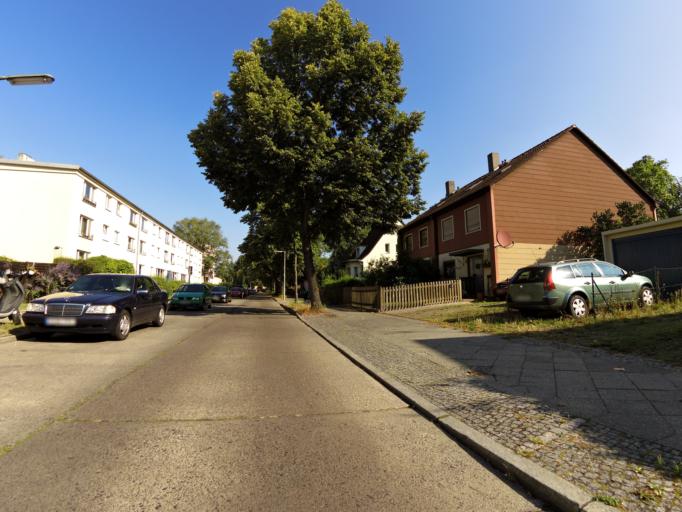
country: DE
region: Berlin
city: Lichtenrade
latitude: 52.3972
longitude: 13.3964
